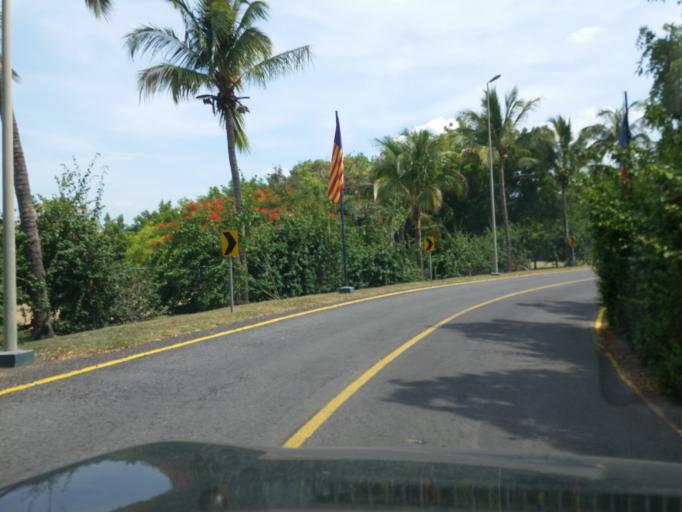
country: NI
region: Managua
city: Masachapa
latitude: 11.8000
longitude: -86.5191
